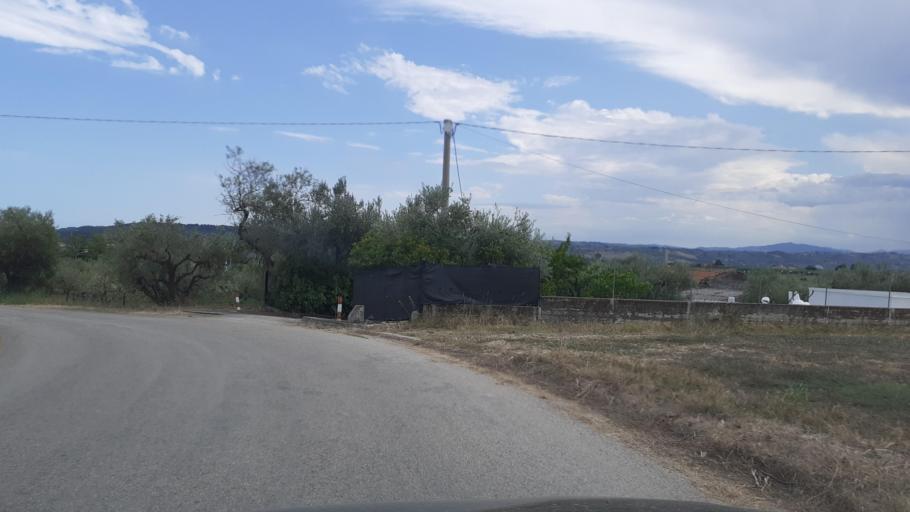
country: IT
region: Abruzzo
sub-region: Provincia di Chieti
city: Fossacesia
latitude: 42.2516
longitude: 14.5020
